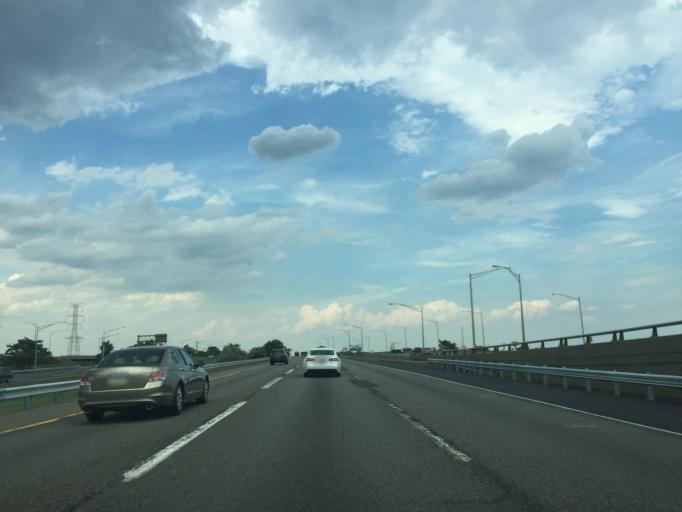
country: US
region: New Jersey
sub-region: Middlesex County
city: Carteret
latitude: 40.5961
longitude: -74.2333
